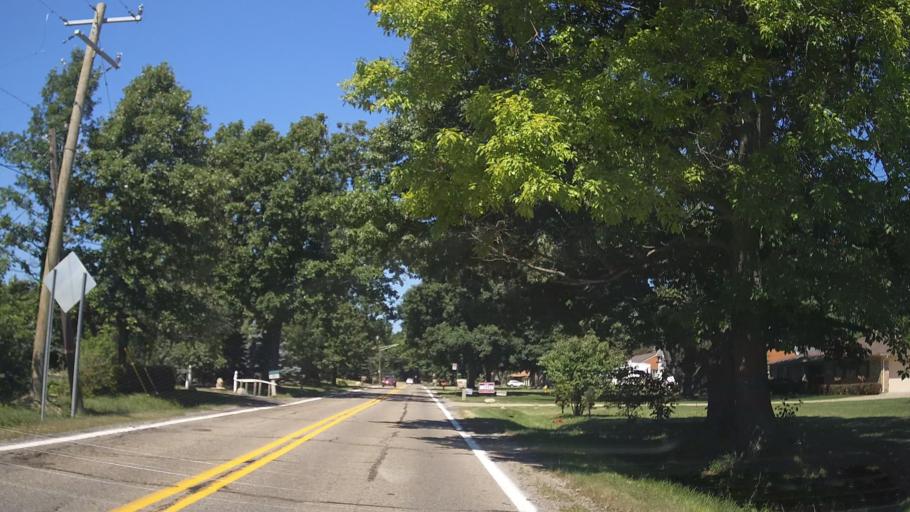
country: US
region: Michigan
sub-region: Macomb County
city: Clinton
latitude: 42.5881
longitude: -82.9054
